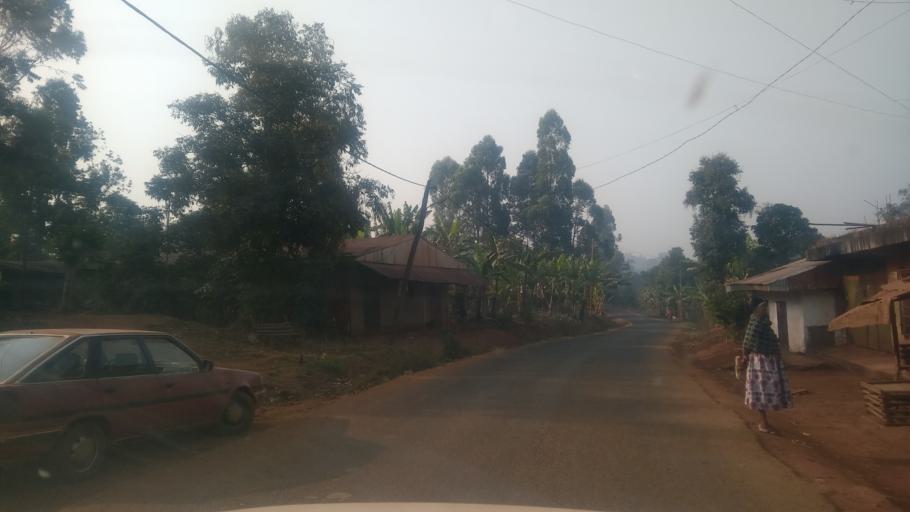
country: CM
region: West
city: Bandjoun
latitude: 5.3456
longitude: 10.4050
